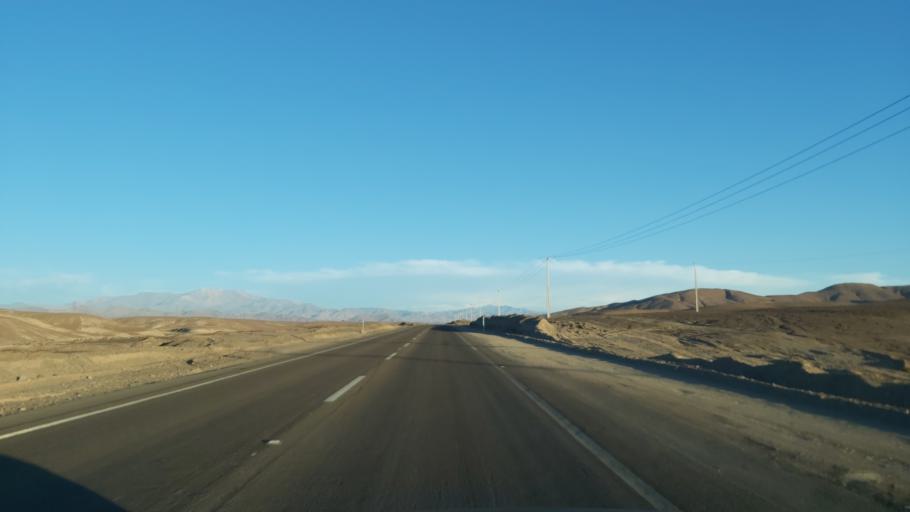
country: CL
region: Atacama
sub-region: Provincia de Chanaral
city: Diego de Almagro
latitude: -26.4296
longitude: -70.0126
